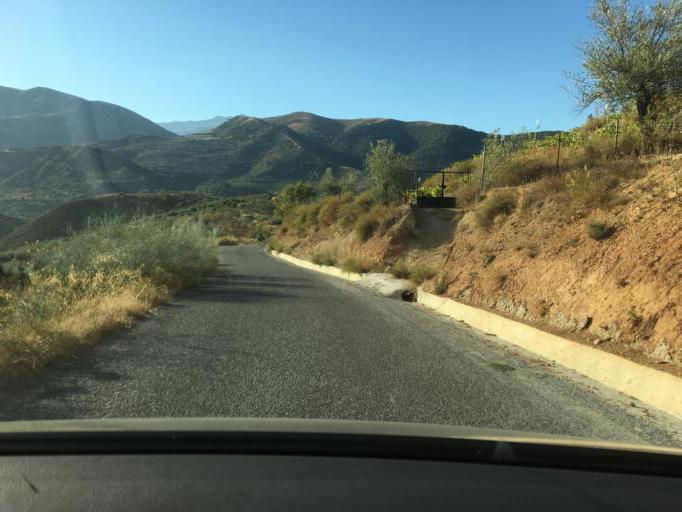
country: ES
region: Andalusia
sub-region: Provincia de Granada
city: Quentar
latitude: 37.2014
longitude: -3.4706
